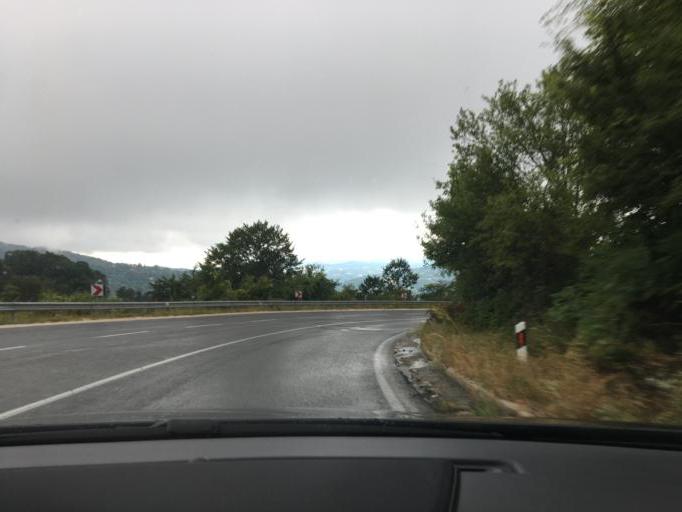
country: MK
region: Kriva Palanka
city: Kriva Palanka
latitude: 42.2164
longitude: 22.4510
